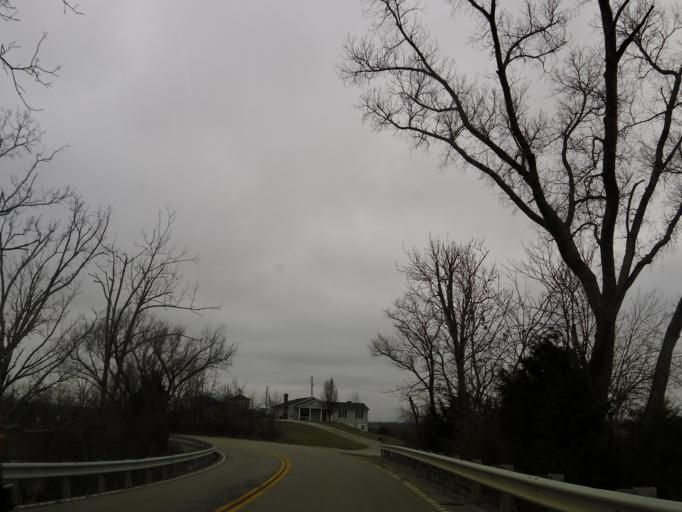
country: US
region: Kentucky
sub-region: Franklin County
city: Frankfort
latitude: 38.2173
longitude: -84.9048
